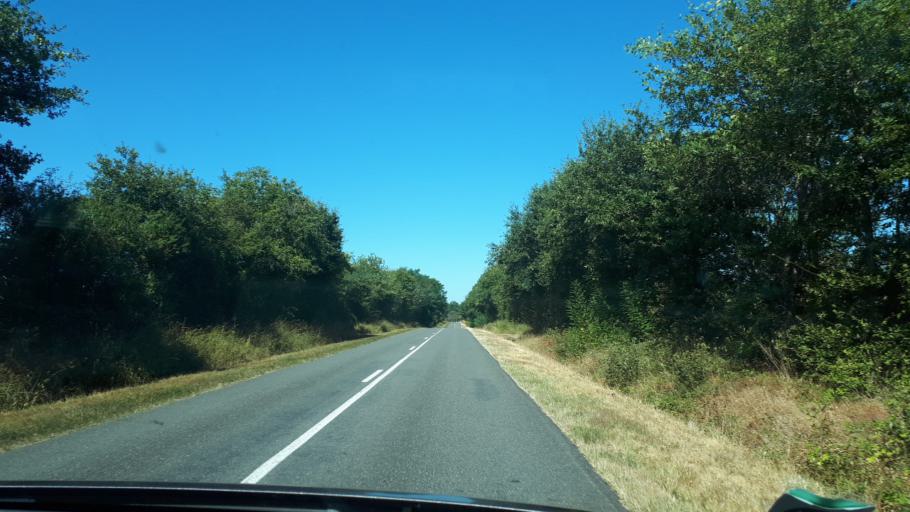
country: FR
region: Centre
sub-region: Departement du Loiret
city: Cerdon
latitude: 47.6398
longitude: 2.4083
